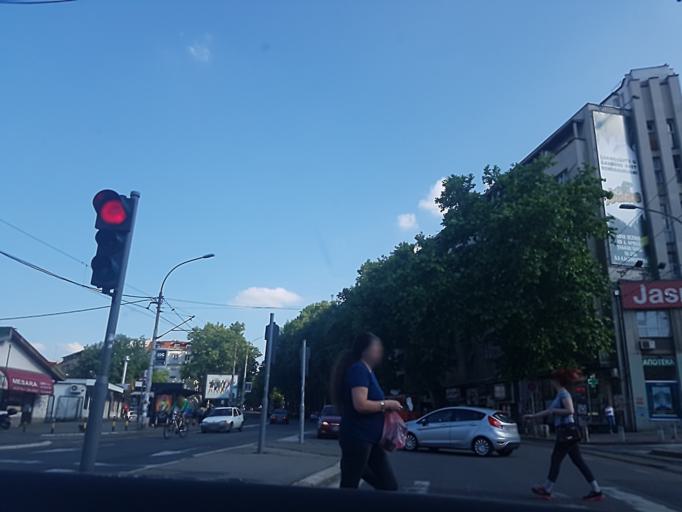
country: RS
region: Central Serbia
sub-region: Belgrade
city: Stari Grad
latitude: 44.8187
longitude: 20.4667
